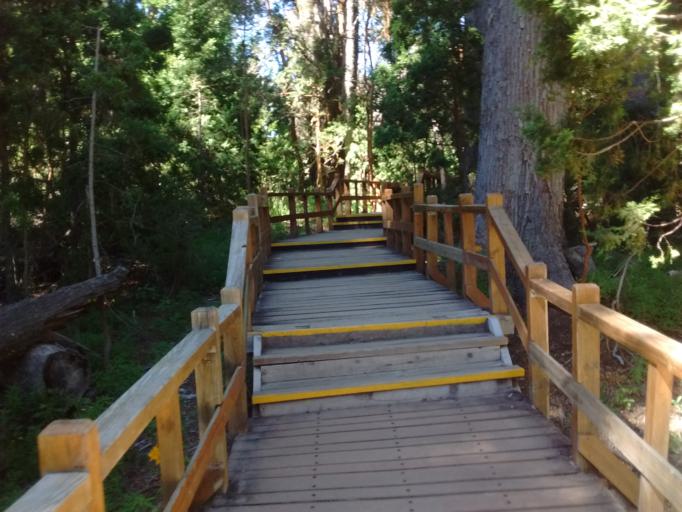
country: AR
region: Neuquen
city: Villa La Angostura
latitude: -40.8564
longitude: -71.6146
